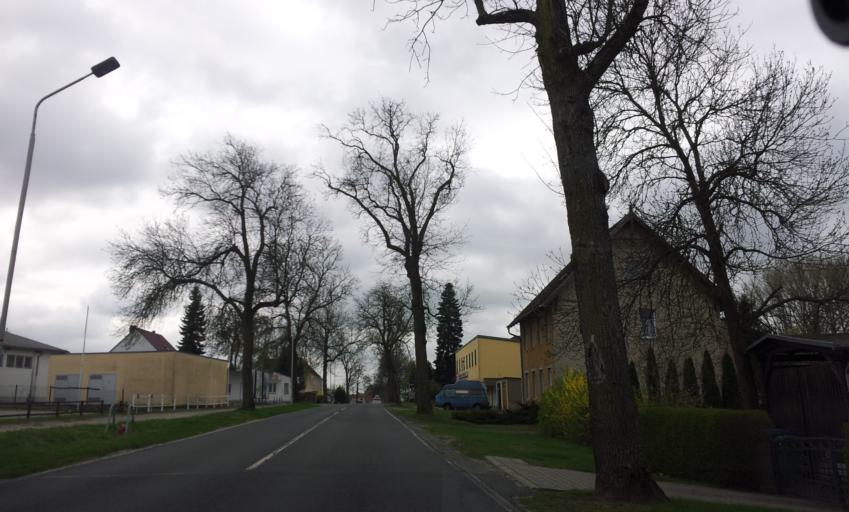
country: DE
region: Brandenburg
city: Juterbog
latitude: 51.9822
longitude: 13.1005
